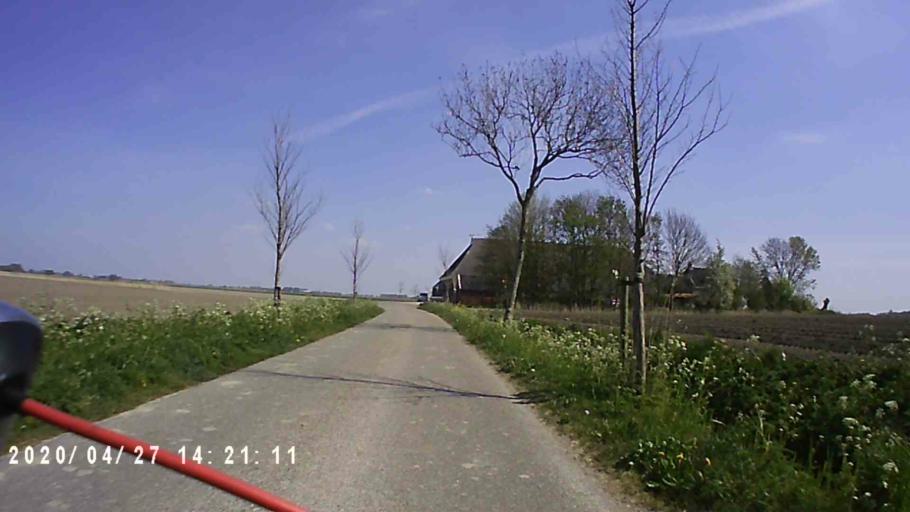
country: NL
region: Groningen
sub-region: Gemeente De Marne
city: Ulrum
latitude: 53.3746
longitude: 6.3834
